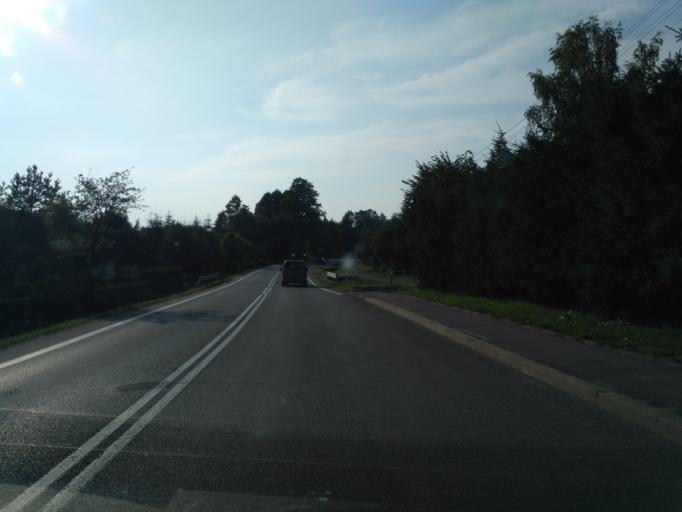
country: PL
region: Subcarpathian Voivodeship
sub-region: Powiat sanocki
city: Strachocina
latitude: 49.6233
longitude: 22.1031
